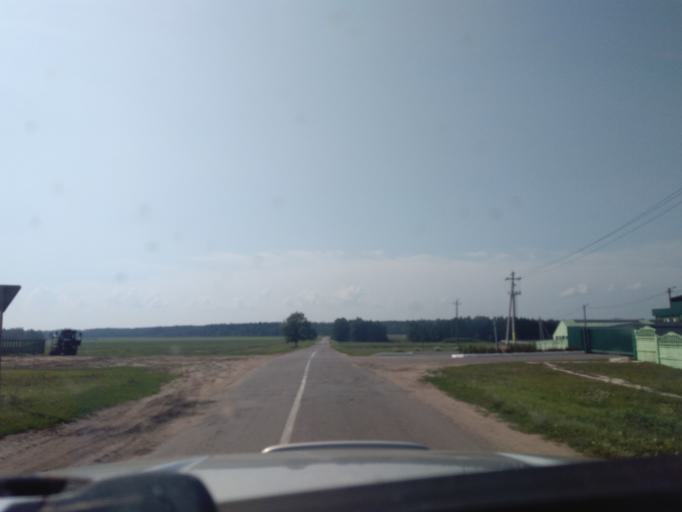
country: BY
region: Minsk
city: Valozhyn
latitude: 54.0379
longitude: 26.6047
